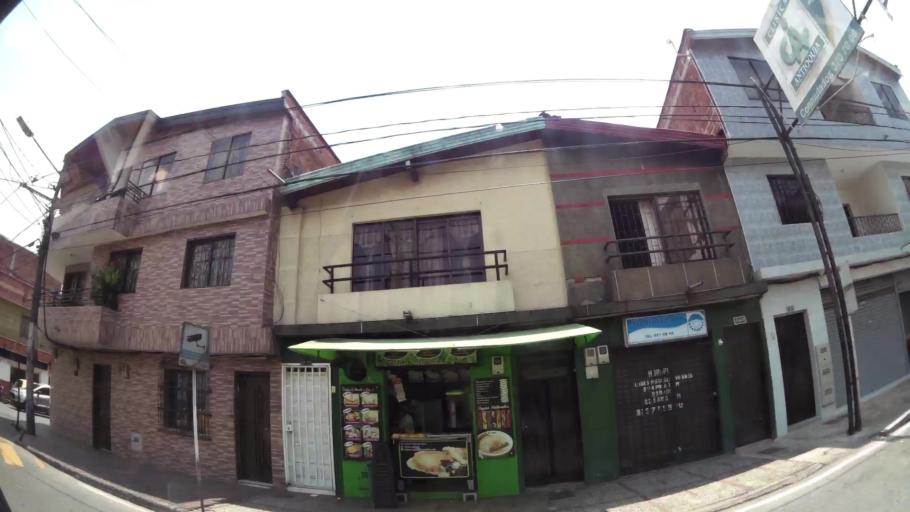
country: CO
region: Antioquia
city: Sabaneta
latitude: 6.1693
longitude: -75.6130
